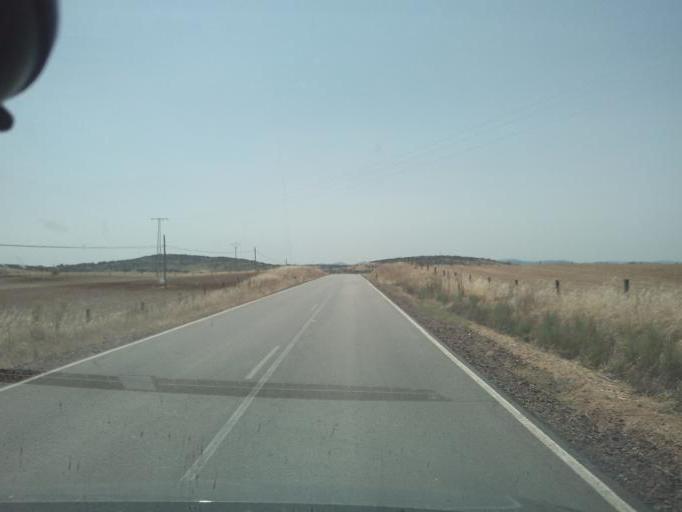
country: ES
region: Extremadura
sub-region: Provincia de Caceres
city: Berrocalejo
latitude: 39.8792
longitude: -5.3423
